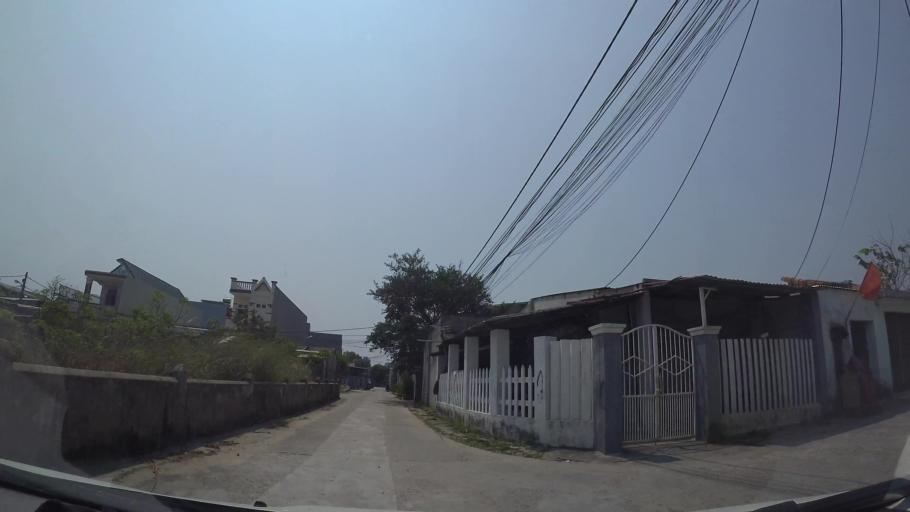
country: VN
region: Da Nang
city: Ngu Hanh Son
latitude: 15.9950
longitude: 108.2663
